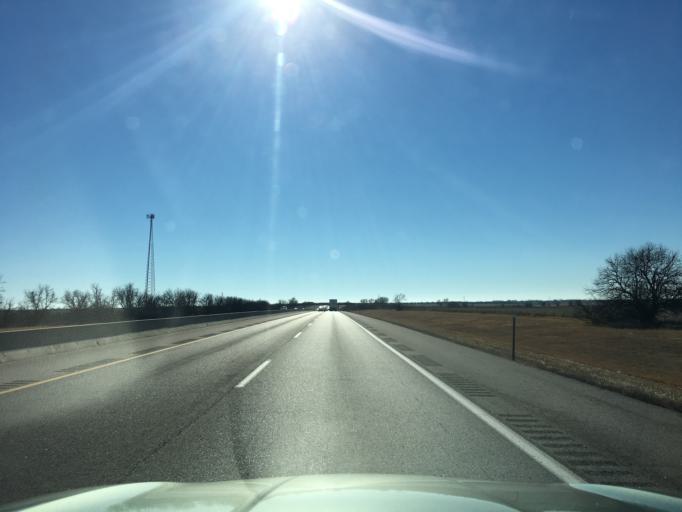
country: US
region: Kansas
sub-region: Sumner County
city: Wellington
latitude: 37.1202
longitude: -97.3389
